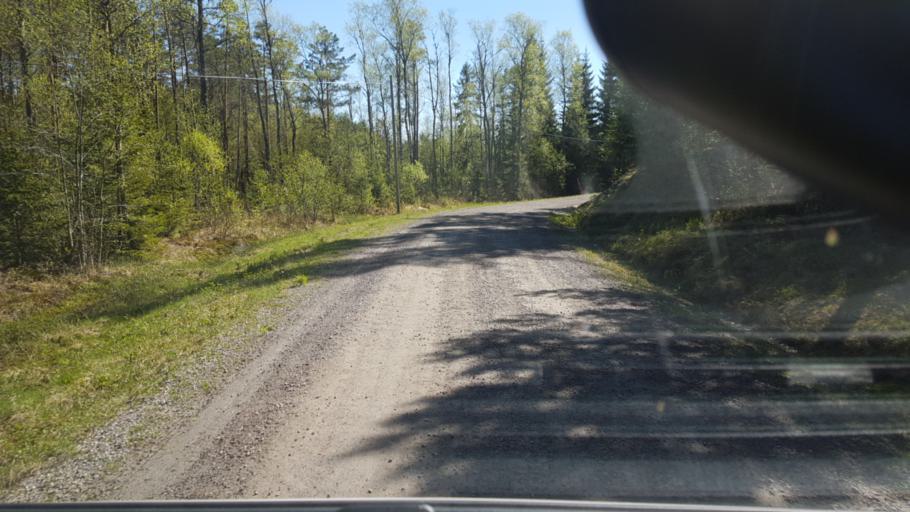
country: SE
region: Vaermland
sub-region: Eda Kommun
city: Charlottenberg
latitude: 59.9093
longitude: 12.3818
